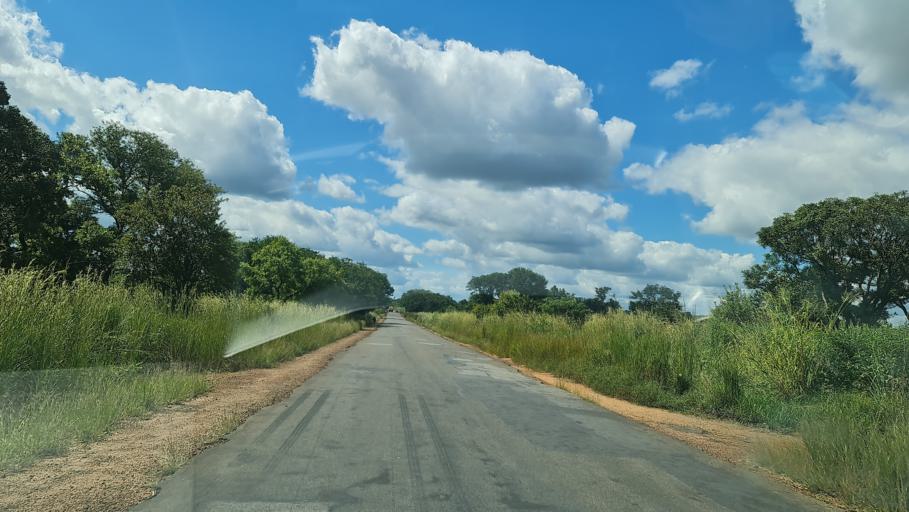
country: MZ
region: Zambezia
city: Quelimane
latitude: -17.5190
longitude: 36.2163
